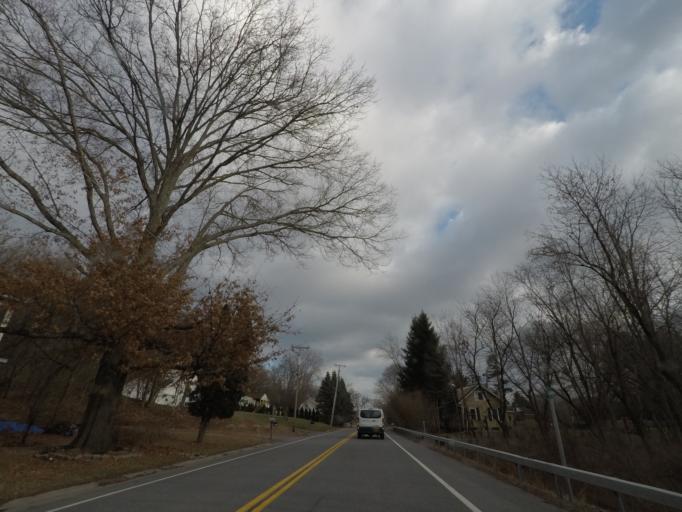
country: US
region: New York
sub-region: Albany County
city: Westmere
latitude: 42.6699
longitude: -73.8863
